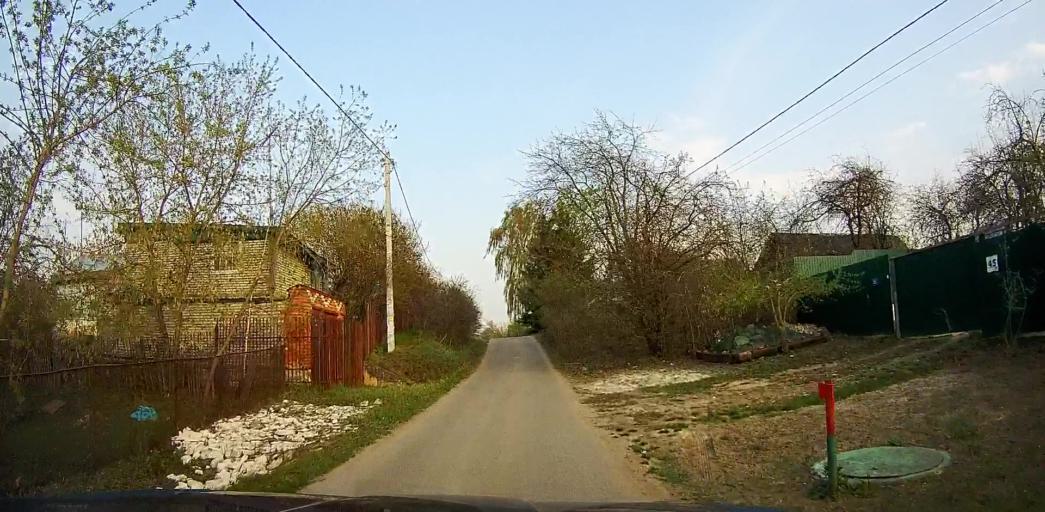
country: RU
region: Moskovskaya
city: Andreyevskoye
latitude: 55.5488
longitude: 37.9570
